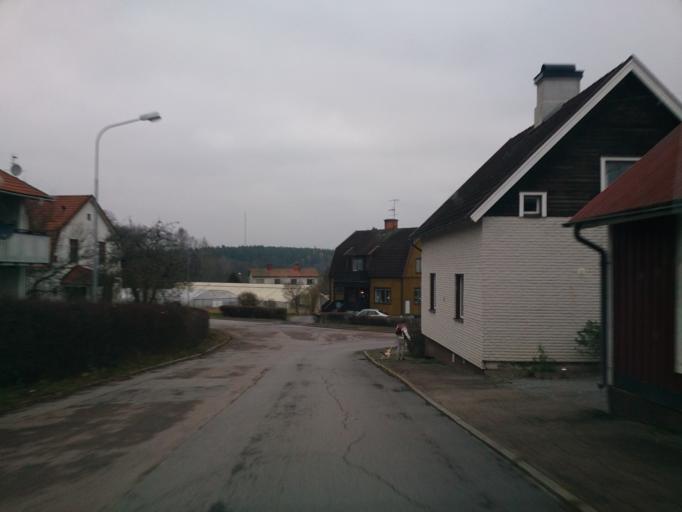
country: SE
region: OEstergoetland
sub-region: Atvidabergs Kommun
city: Atvidaberg
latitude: 58.1949
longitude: 16.0129
